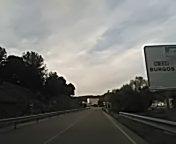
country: ES
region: Castille and Leon
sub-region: Provincia de Soria
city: San Leonardo de Yague
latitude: 41.8342
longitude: -3.0828
